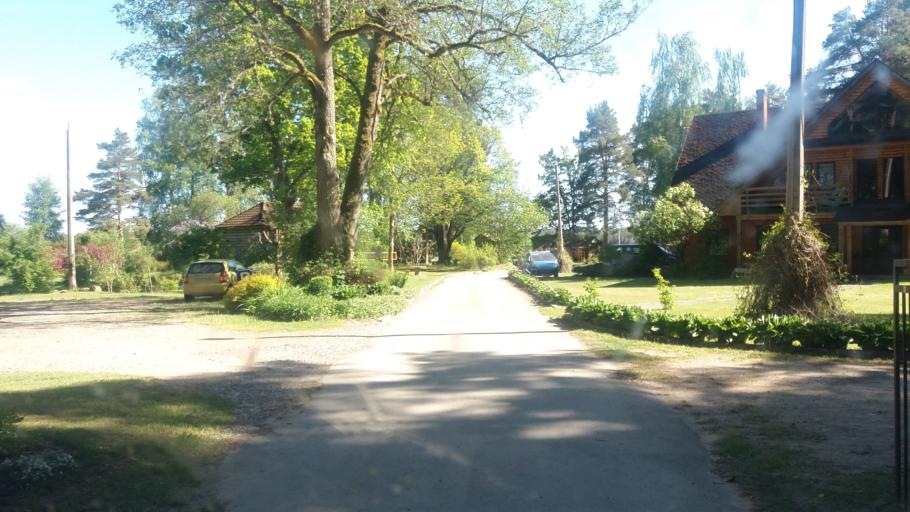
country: LV
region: Kuldigas Rajons
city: Kuldiga
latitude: 57.0759
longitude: 21.8132
